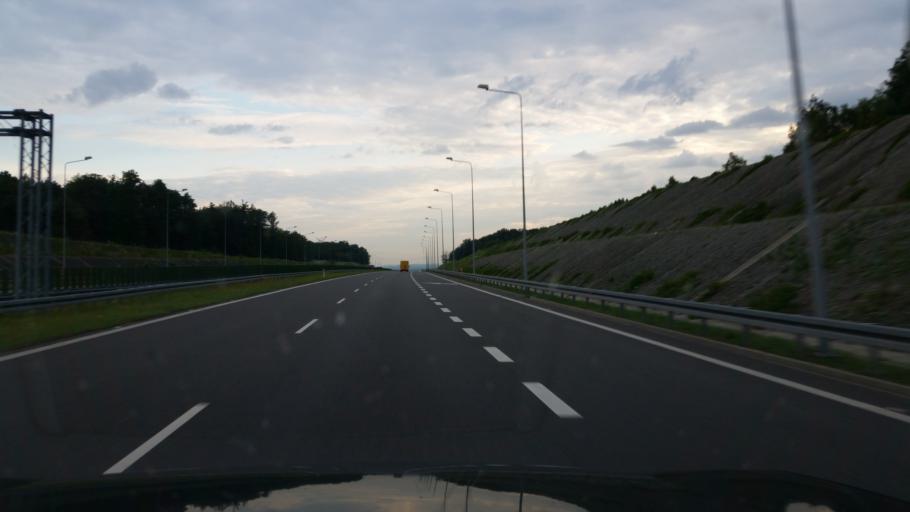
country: PL
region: Silesian Voivodeship
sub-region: Powiat wodzislawski
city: Laziska
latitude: 49.9443
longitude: 18.4272
